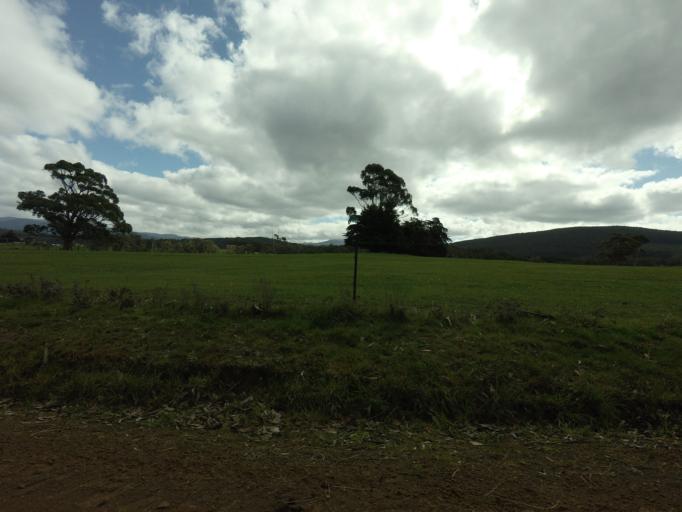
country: AU
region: Tasmania
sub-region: Huon Valley
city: Geeveston
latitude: -43.4323
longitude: 146.9892
